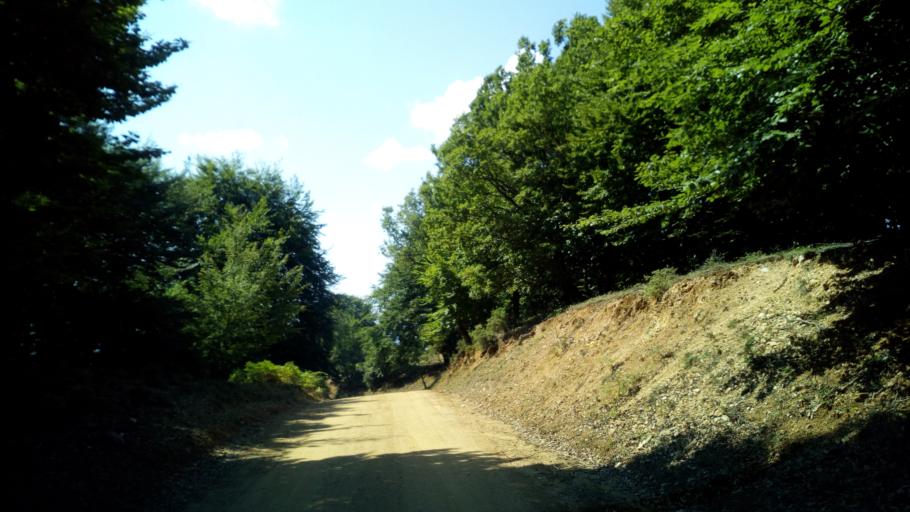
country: GR
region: Central Macedonia
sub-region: Nomos Thessalonikis
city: Sochos
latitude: 40.8285
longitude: 23.3417
